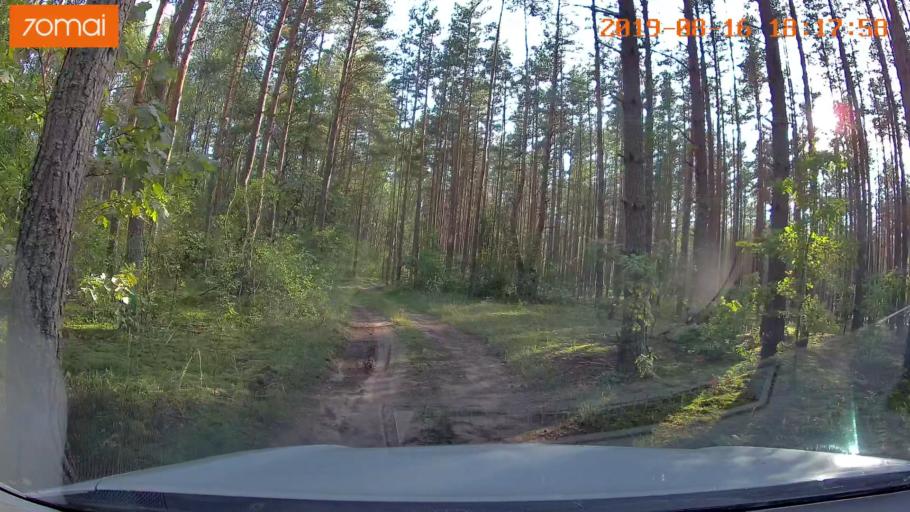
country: BY
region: Mogilev
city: Asipovichy
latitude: 53.2107
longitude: 28.6366
